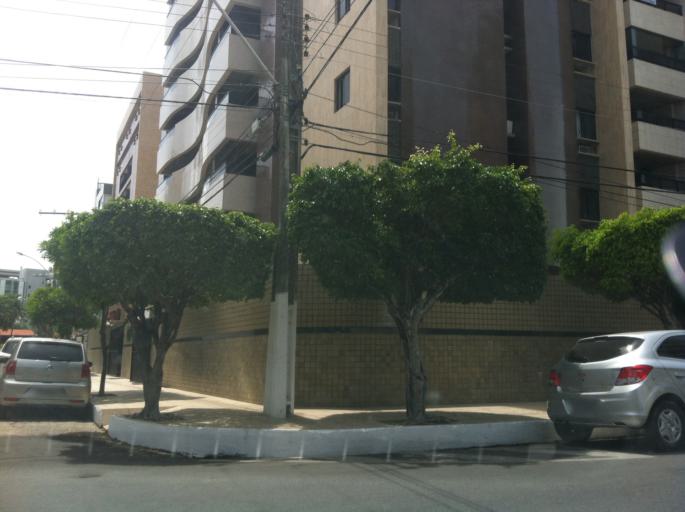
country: BR
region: Alagoas
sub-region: Maceio
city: Maceio
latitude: -9.6627
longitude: -35.7055
